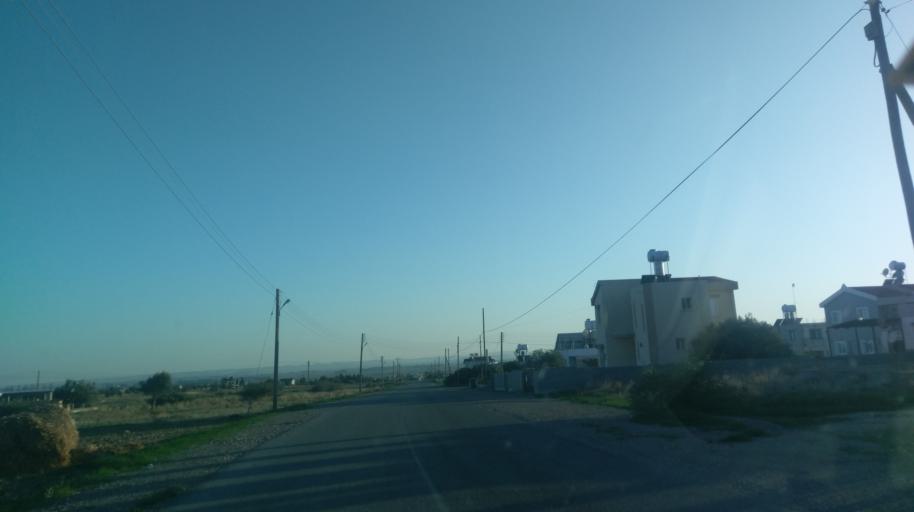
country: CY
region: Ammochostos
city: Lefkonoiko
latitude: 35.2409
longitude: 33.5545
